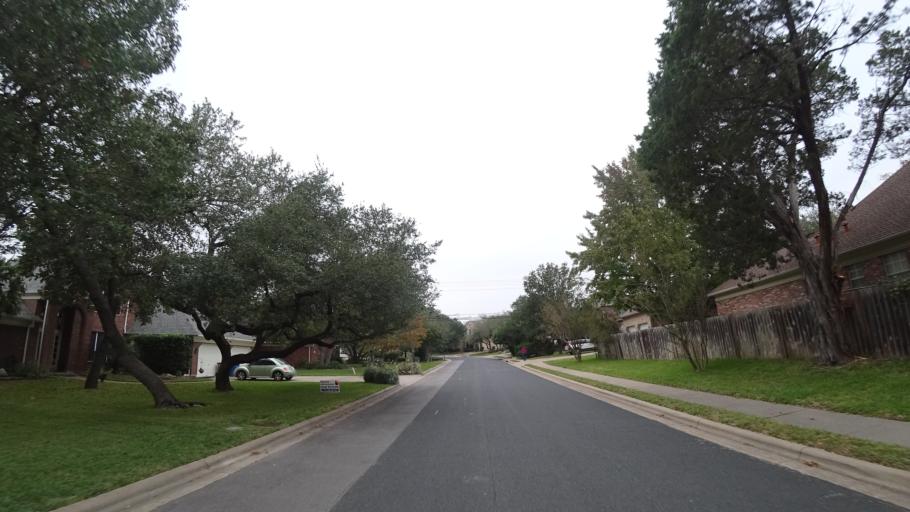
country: US
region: Texas
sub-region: Travis County
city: Shady Hollow
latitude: 30.1859
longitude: -97.8986
